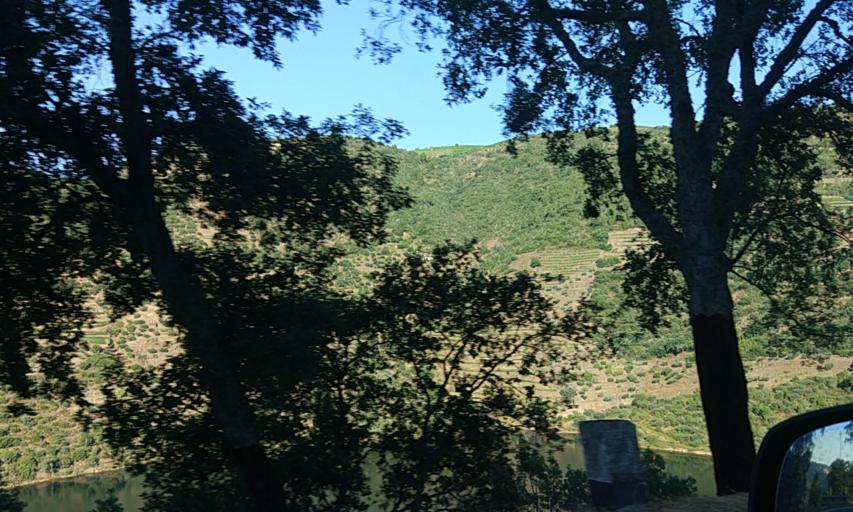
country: PT
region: Viseu
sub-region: Sao Joao da Pesqueira
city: Sao Joao da Pesqueira
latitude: 41.2261
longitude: -7.4255
